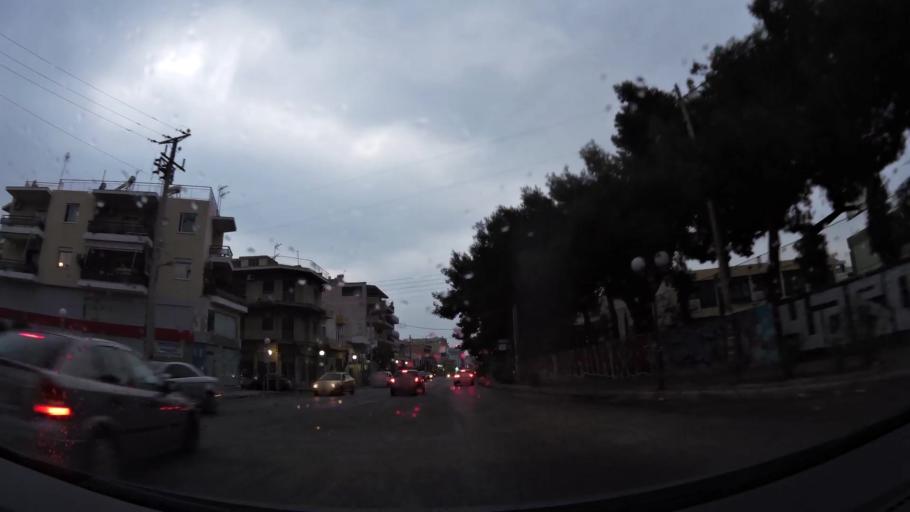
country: GR
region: Attica
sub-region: Nomarchia Athinas
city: Ymittos
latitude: 37.9463
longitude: 23.7471
